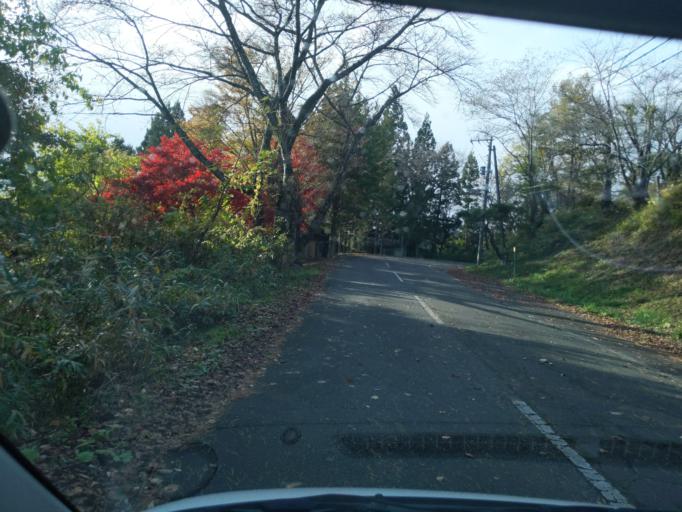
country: JP
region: Iwate
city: Ichinoseki
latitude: 39.0187
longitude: 141.1058
